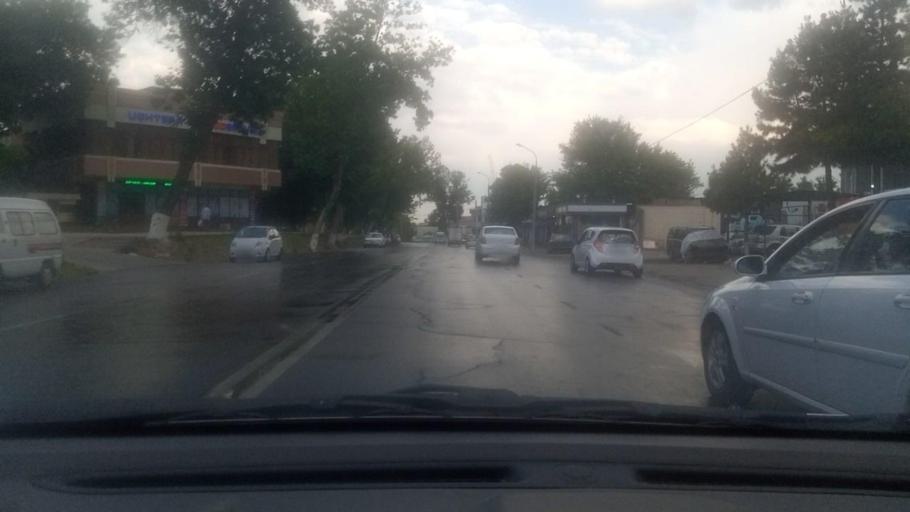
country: UZ
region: Toshkent Shahri
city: Tashkent
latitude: 41.2984
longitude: 69.1889
